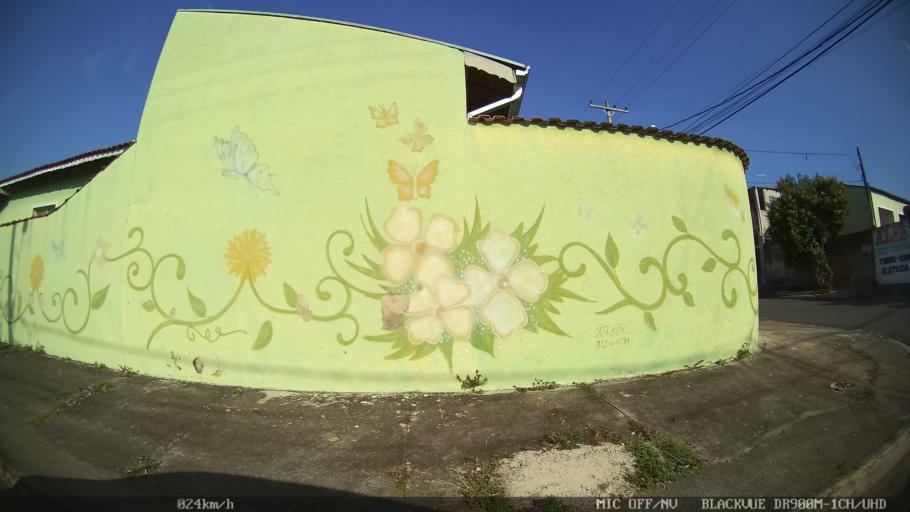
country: BR
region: Sao Paulo
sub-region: Indaiatuba
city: Indaiatuba
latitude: -22.9864
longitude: -47.1531
